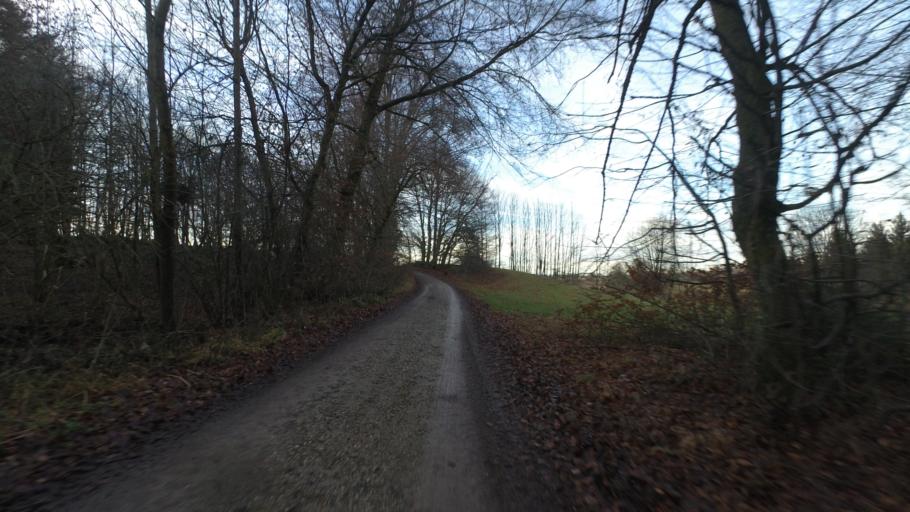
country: DE
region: Bavaria
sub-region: Upper Bavaria
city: Chieming
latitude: 47.8818
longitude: 12.5536
